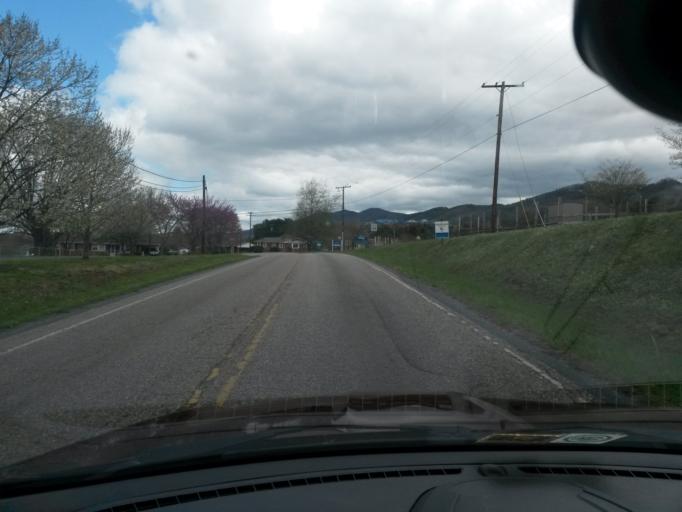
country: US
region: Virginia
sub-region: City of Buena Vista
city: Buena Vista
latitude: 37.7146
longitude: -79.3661
